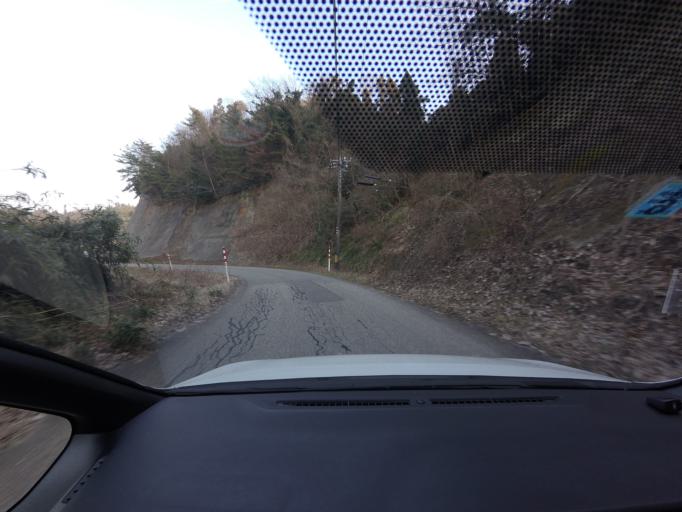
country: JP
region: Ishikawa
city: Nanao
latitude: 37.1435
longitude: 137.0180
